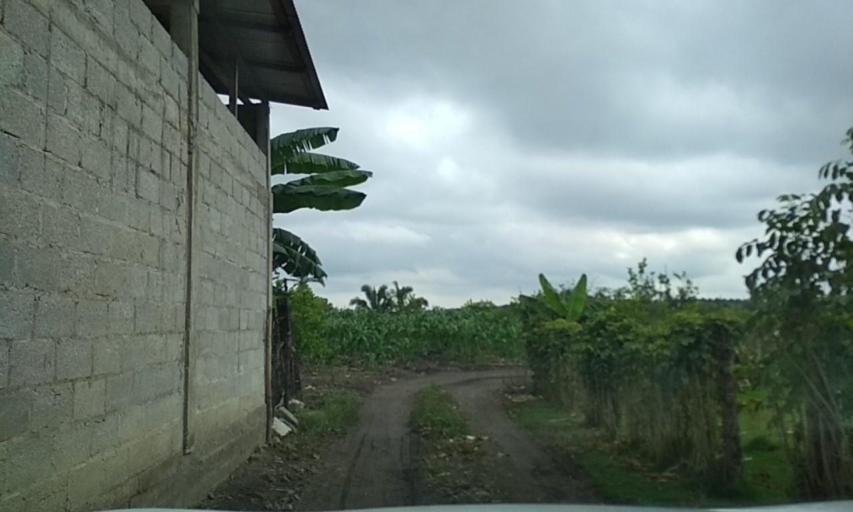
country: MX
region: Veracruz
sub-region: Papantla
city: El Chote
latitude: 20.3639
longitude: -97.4293
